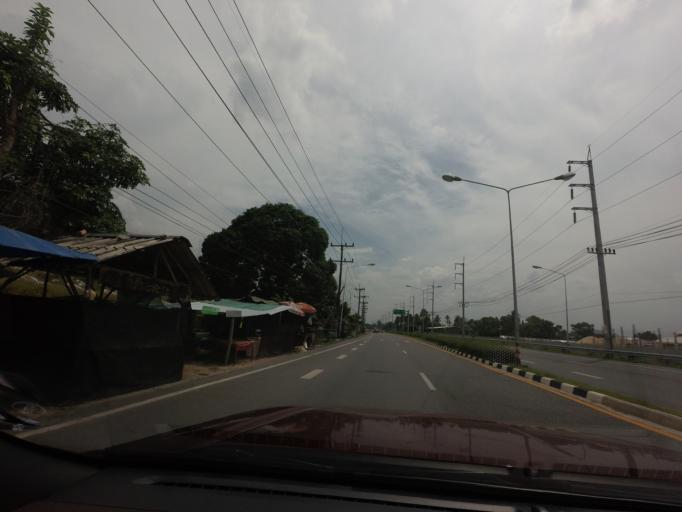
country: TH
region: Yala
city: Yala
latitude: 6.5013
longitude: 101.2732
